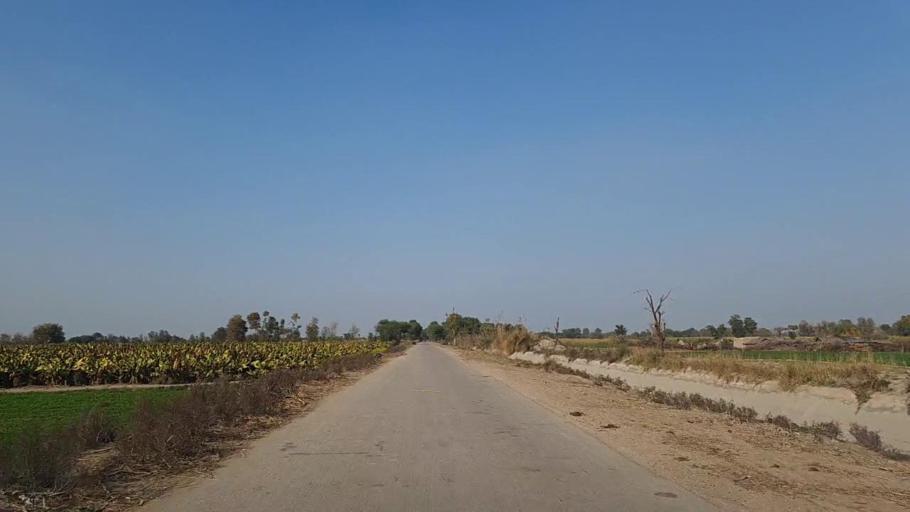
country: PK
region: Sindh
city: Daur
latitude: 26.4086
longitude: 68.2592
